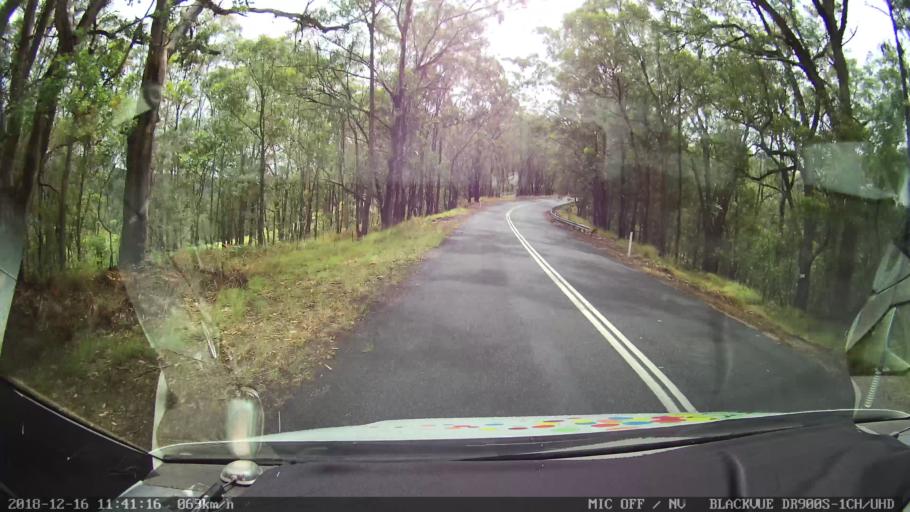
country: AU
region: New South Wales
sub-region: Tenterfield Municipality
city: Carrolls Creek
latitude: -28.9585
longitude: 152.2071
